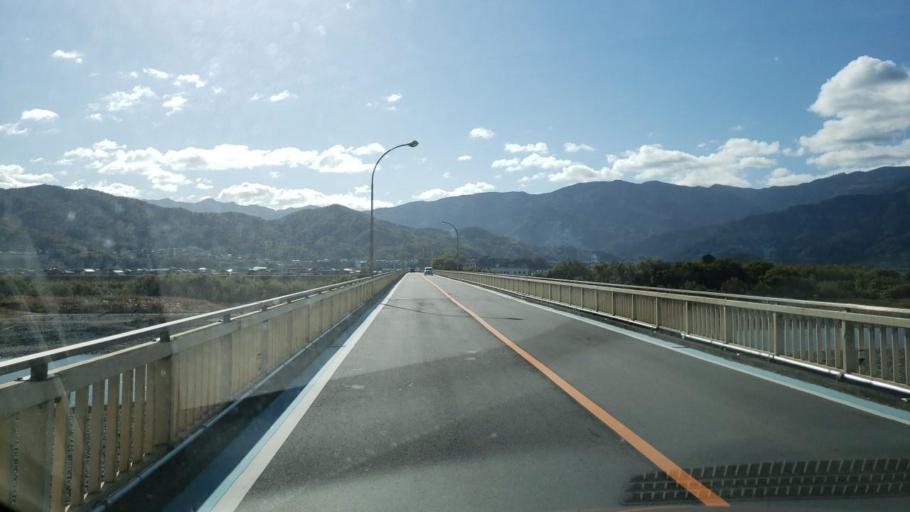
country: JP
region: Tokushima
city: Wakimachi
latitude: 34.0707
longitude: 134.2368
